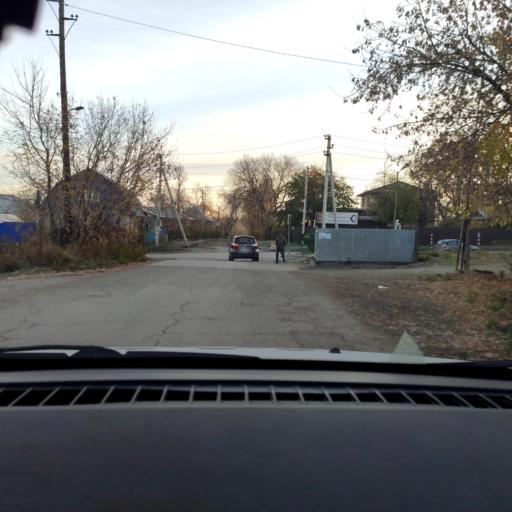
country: RU
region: Perm
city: Perm
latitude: 58.0344
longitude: 56.3213
